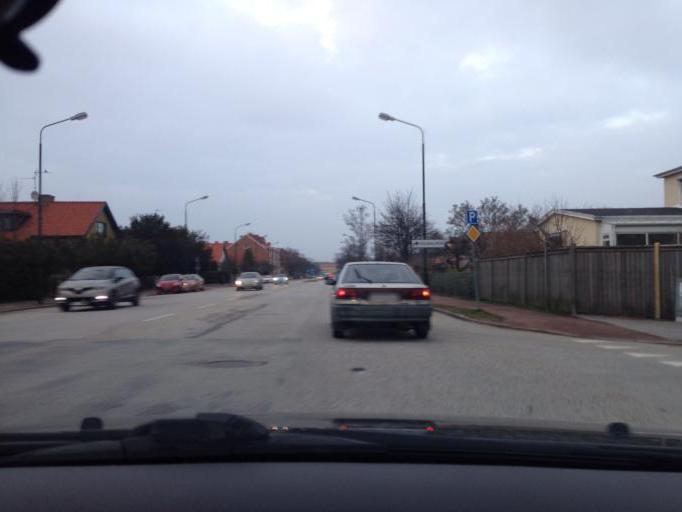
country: SE
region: Skane
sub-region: Malmo
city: Malmoe
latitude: 55.5875
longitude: 12.9701
